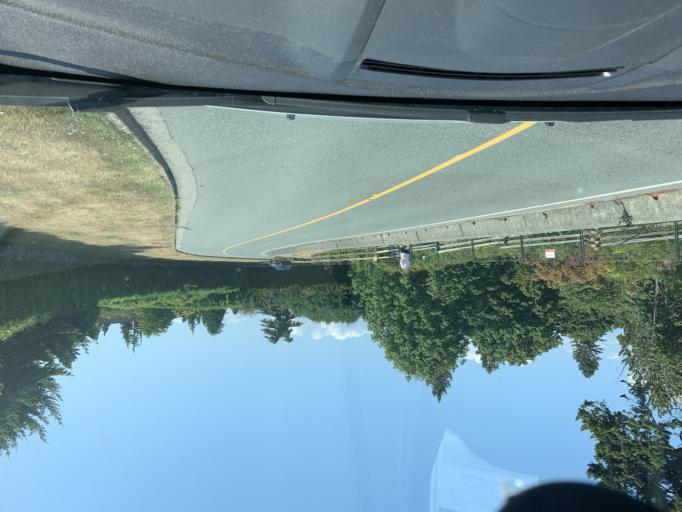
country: CA
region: British Columbia
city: West End
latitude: 49.2753
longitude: -123.2515
